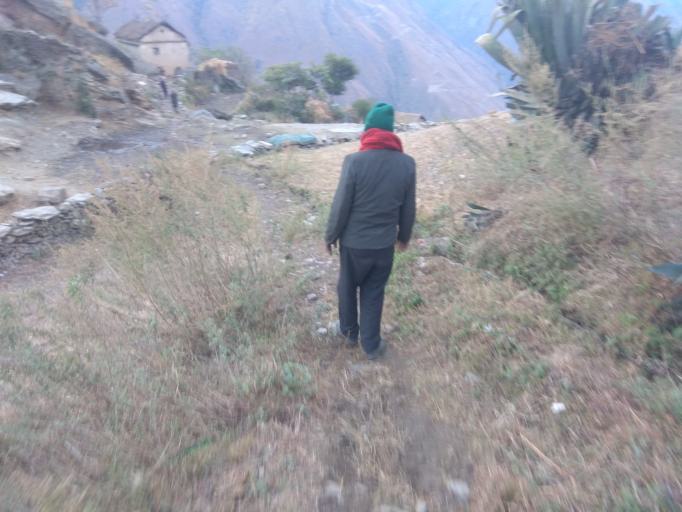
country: NP
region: Mid Western
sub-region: Bheri Zone
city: Dailekh
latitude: 29.2839
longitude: 81.7195
